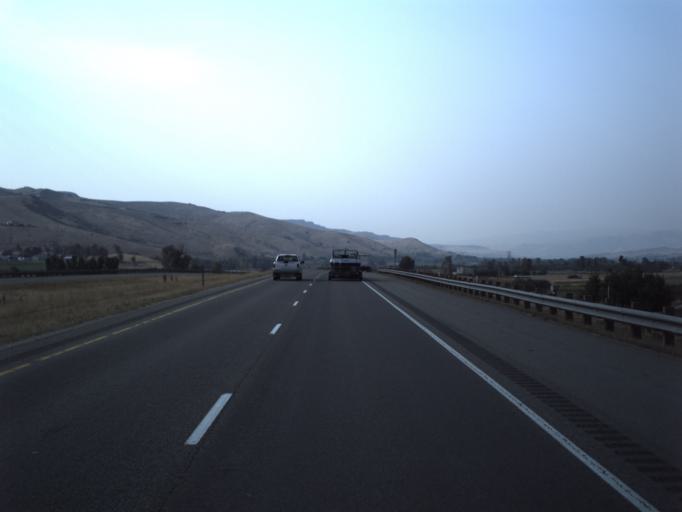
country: US
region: Utah
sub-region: Summit County
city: Coalville
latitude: 40.8466
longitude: -111.3881
